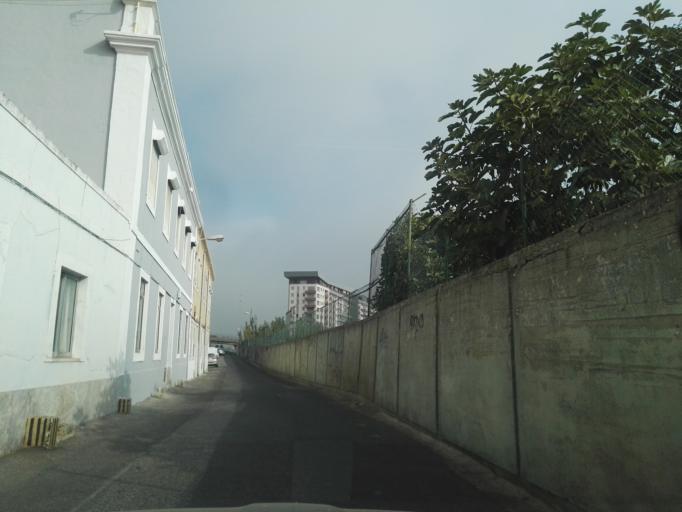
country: PT
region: Lisbon
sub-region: Loures
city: Moscavide
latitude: 38.7530
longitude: -9.1005
